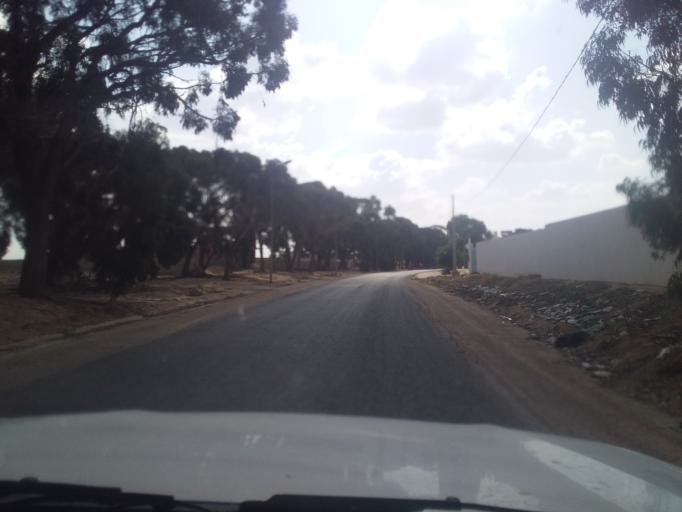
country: TN
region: Qabis
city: Gabes
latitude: 33.6256
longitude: 10.2748
